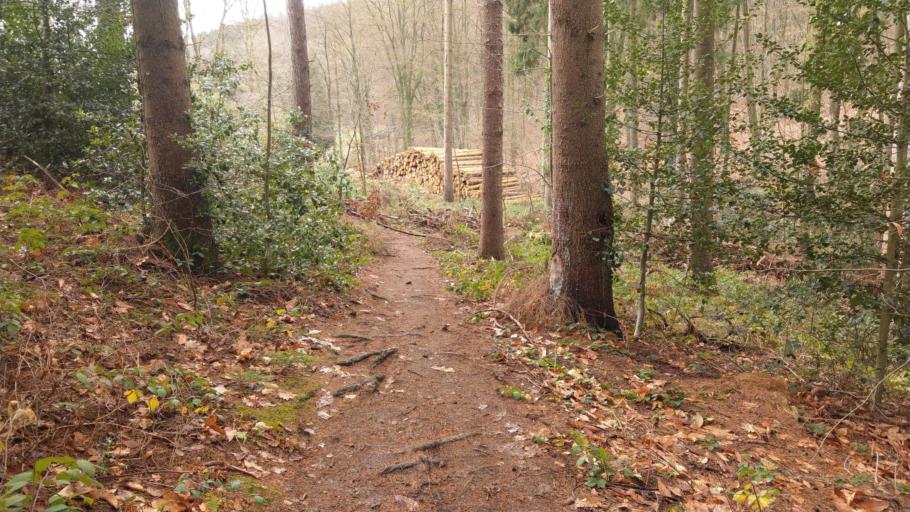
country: NL
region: Limburg
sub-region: Gemeente Vaals
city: Vaals
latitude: 50.7520
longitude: 6.0500
